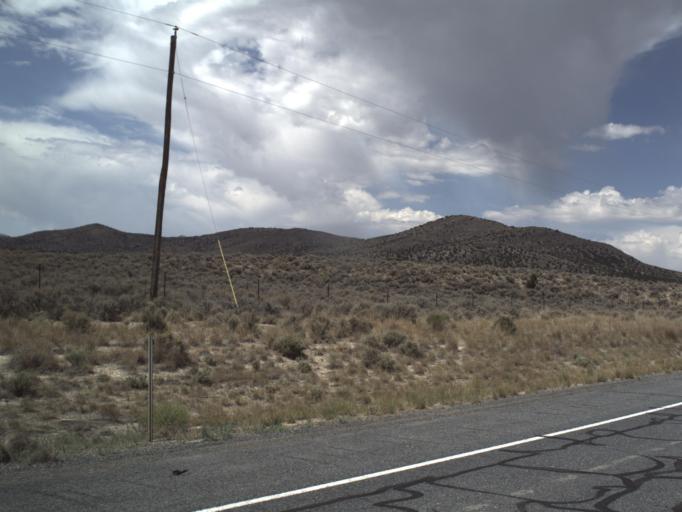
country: US
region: Utah
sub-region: Utah County
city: Eagle Mountain
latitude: 40.0762
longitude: -112.3444
